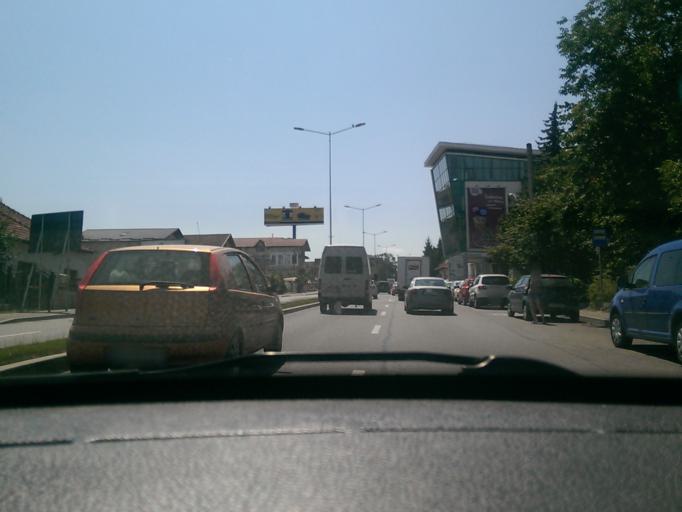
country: RO
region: Cluj
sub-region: Municipiul Cluj-Napoca
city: Cluj-Napoca
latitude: 46.7551
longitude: 23.5961
